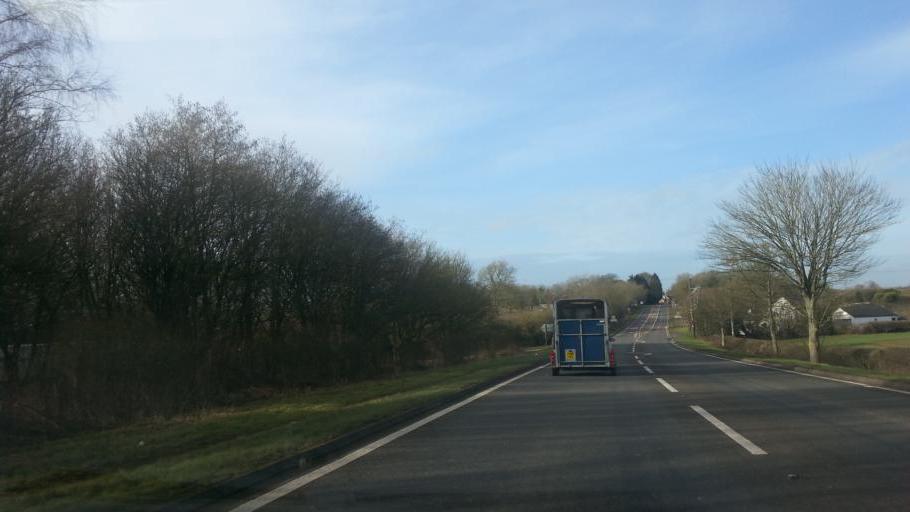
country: GB
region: England
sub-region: District of Rutland
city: Ridlington
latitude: 52.5995
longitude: -0.8706
